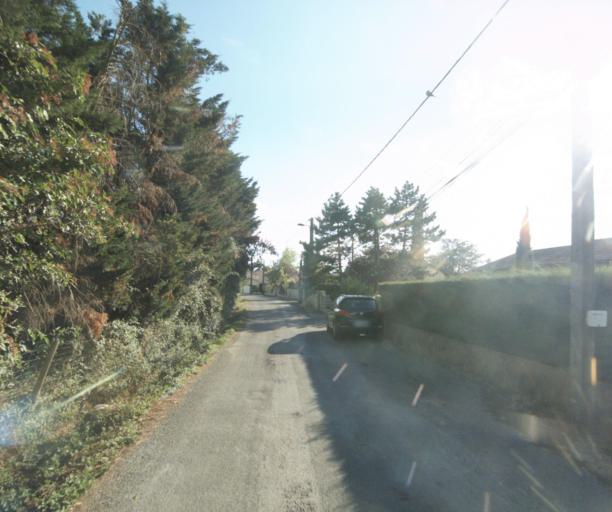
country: FR
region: Rhone-Alpes
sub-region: Departement du Rhone
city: Lentilly
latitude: 45.8314
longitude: 4.6781
